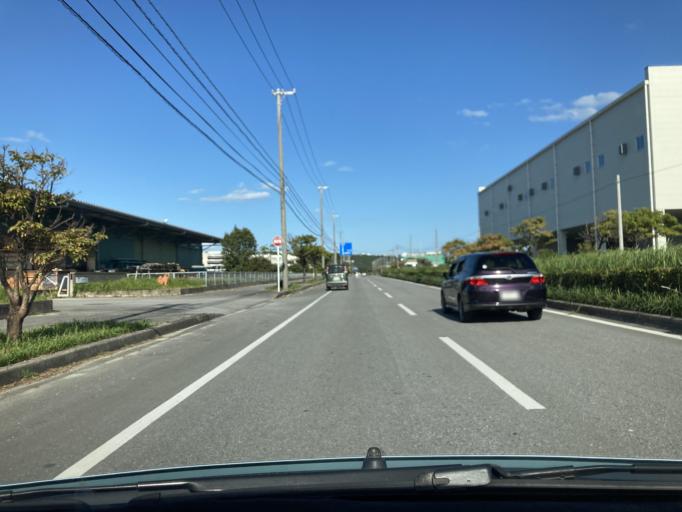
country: JP
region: Okinawa
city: Katsuren-haebaru
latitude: 26.3377
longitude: 127.8528
